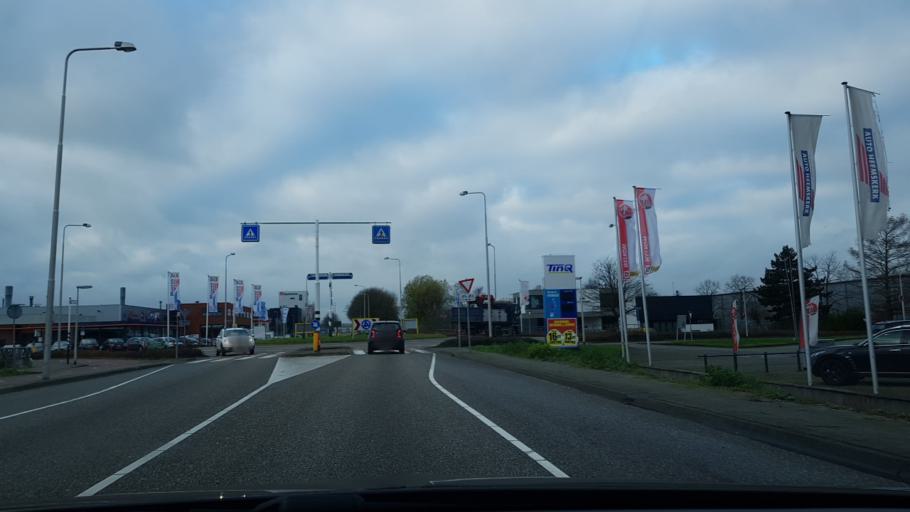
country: NL
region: South Holland
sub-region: Gemeente Kaag en Braassem
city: Oude Wetering
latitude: 52.2035
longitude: 4.6238
